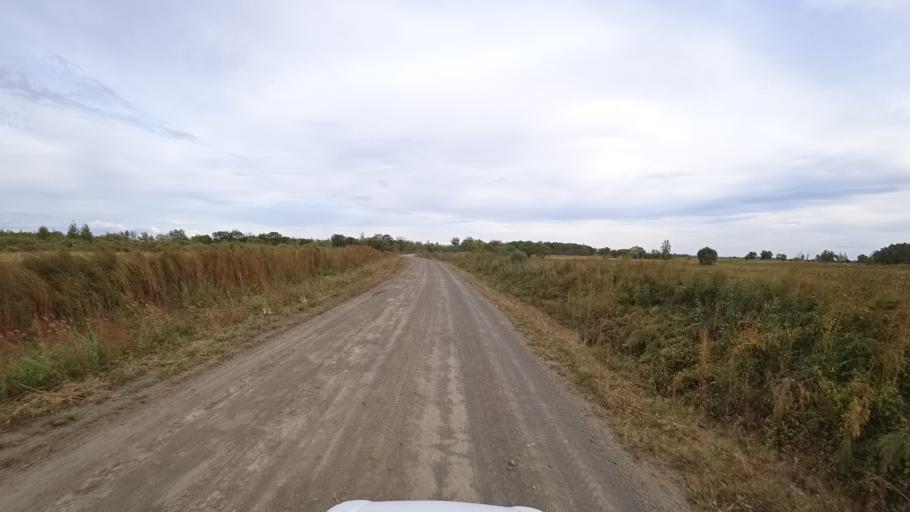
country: RU
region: Amur
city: Arkhara
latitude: 49.3535
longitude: 130.1457
